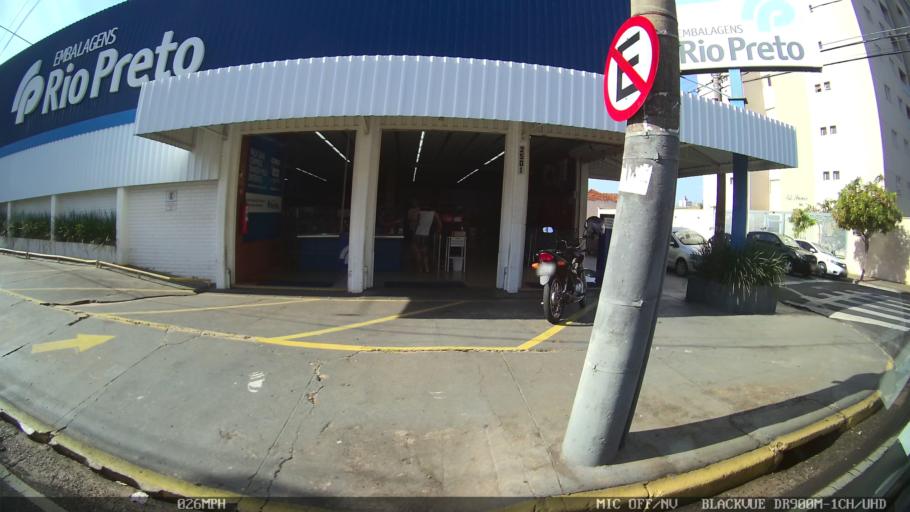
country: BR
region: Sao Paulo
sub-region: Sao Jose Do Rio Preto
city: Sao Jose do Rio Preto
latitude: -20.8065
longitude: -49.3817
